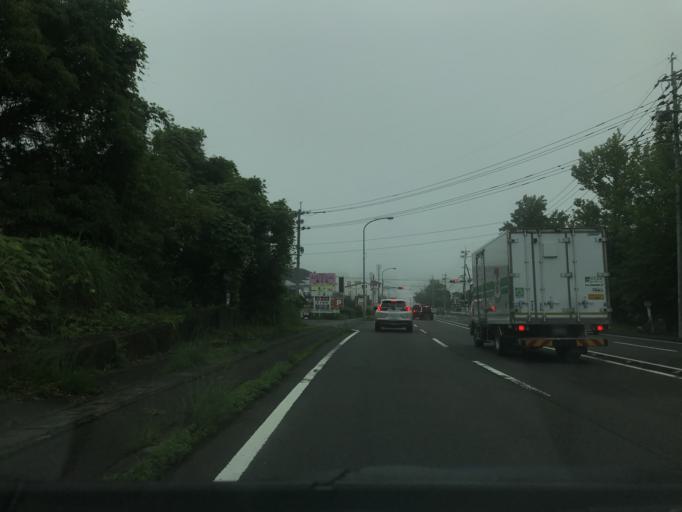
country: JP
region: Oita
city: Beppu
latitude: 33.3005
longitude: 131.4613
